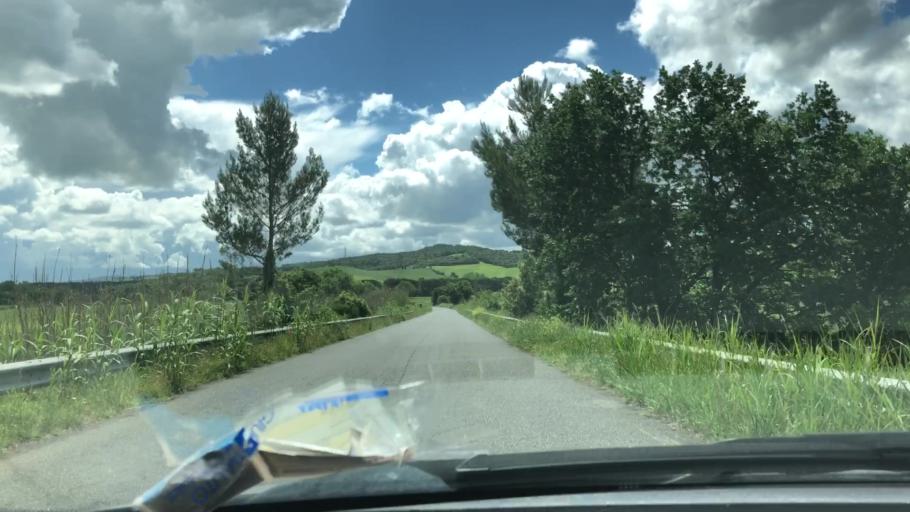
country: IT
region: Tuscany
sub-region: Province of Pisa
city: Saline
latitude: 43.3532
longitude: 10.7867
